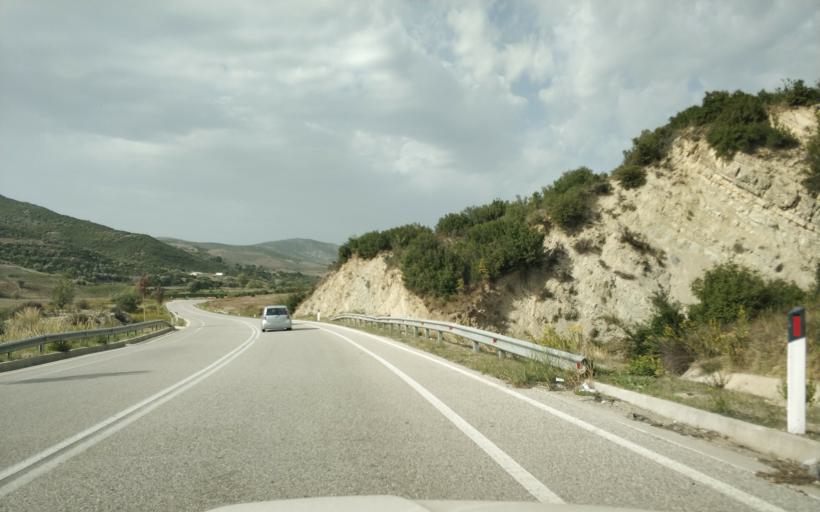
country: AL
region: Gjirokaster
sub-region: Rrethi i Tepelenes
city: Krahes
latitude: 40.4027
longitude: 19.8633
